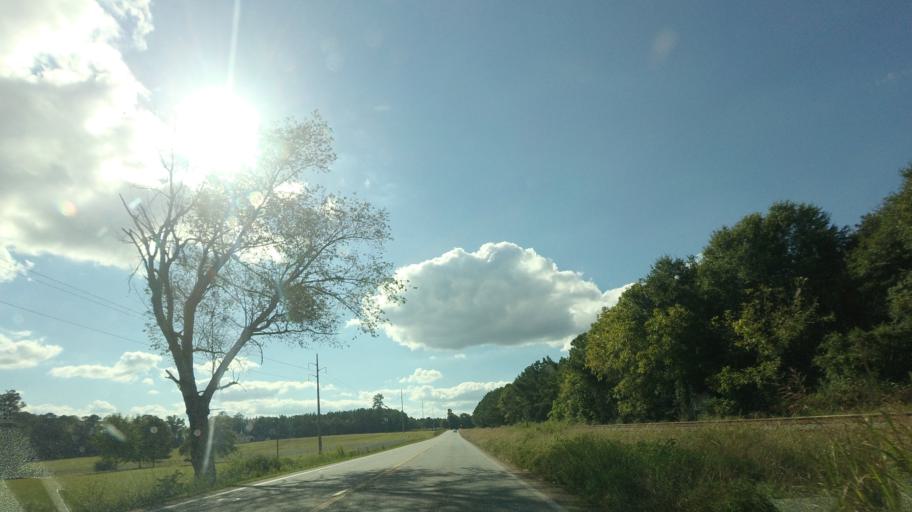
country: US
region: Georgia
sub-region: Monroe County
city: Forsyth
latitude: 33.0473
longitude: -84.0198
